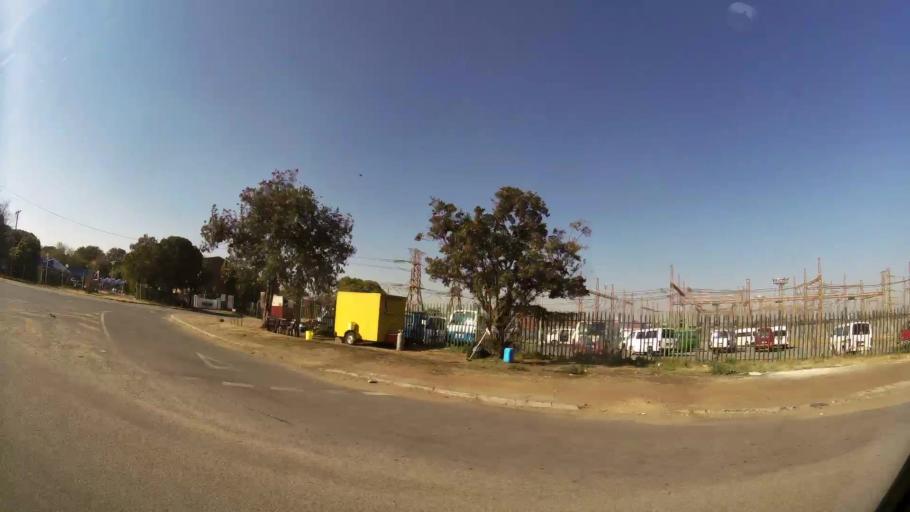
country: ZA
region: Gauteng
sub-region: Ekurhuleni Metropolitan Municipality
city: Germiston
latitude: -26.2278
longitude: 28.1147
